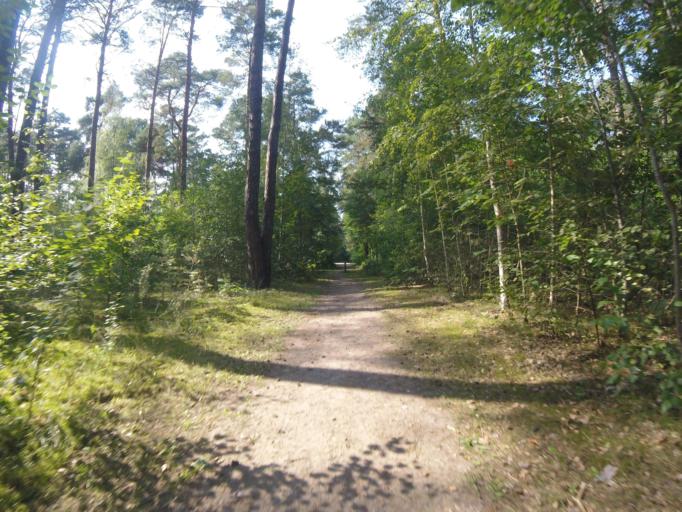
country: DE
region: Brandenburg
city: Bestensee
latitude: 52.2650
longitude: 13.7439
